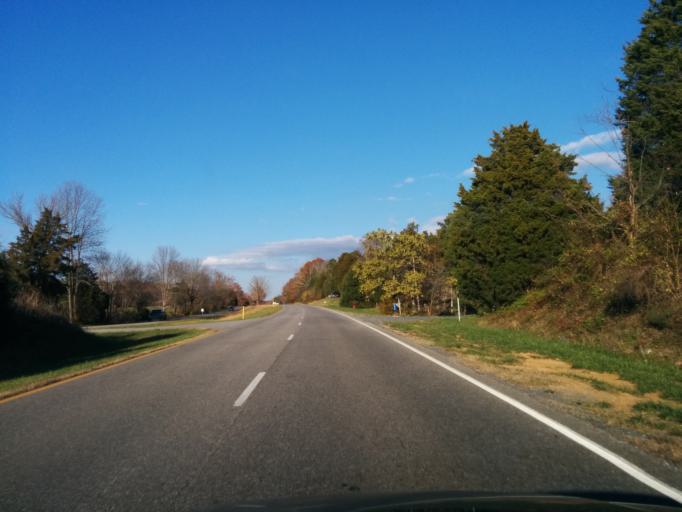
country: US
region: Virginia
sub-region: Rockbridge County
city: East Lexington
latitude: 37.8171
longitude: -79.3938
